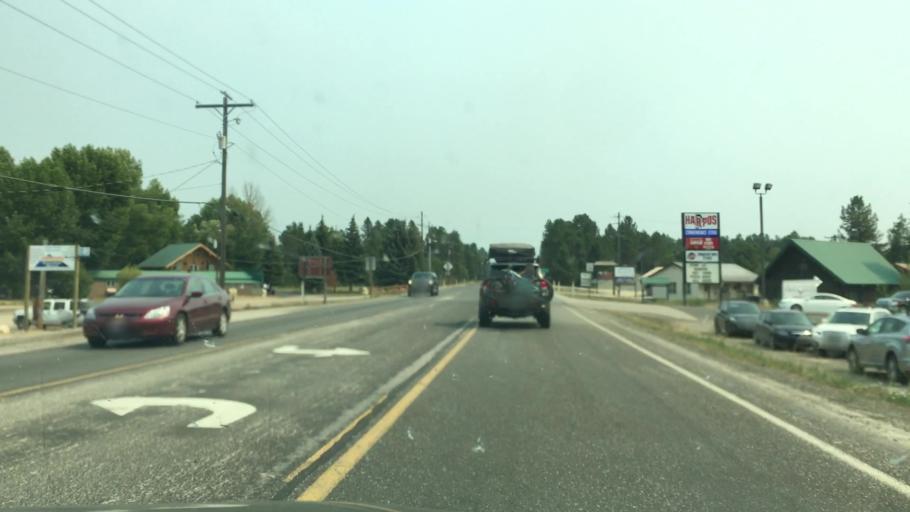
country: US
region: Idaho
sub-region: Valley County
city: Cascade
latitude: 44.5051
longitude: -116.0295
